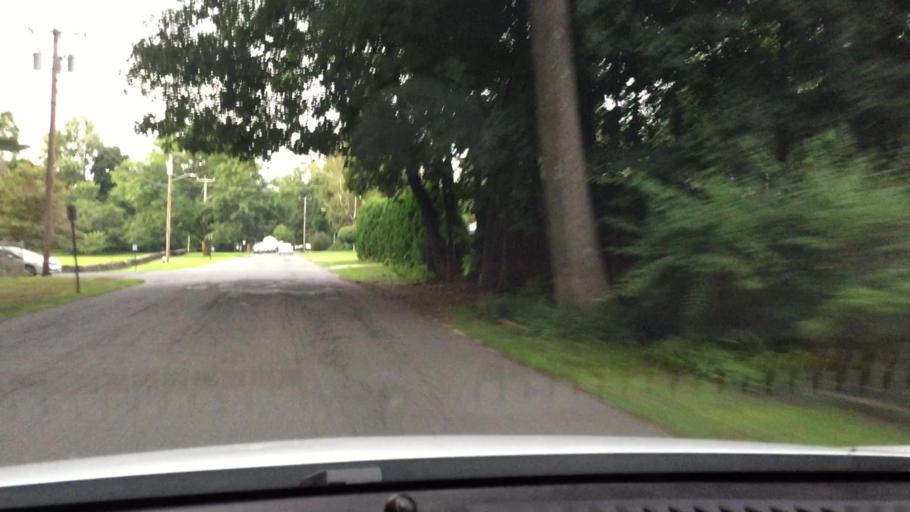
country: US
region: Massachusetts
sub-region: Hampden County
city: Westfield
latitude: 42.1227
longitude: -72.7815
